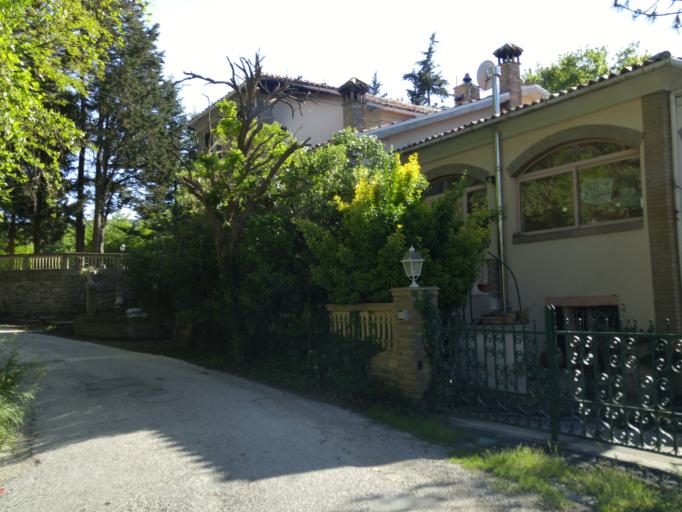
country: IT
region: The Marches
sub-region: Provincia di Pesaro e Urbino
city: Mombaroccio
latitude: 43.8113
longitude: 12.8415
